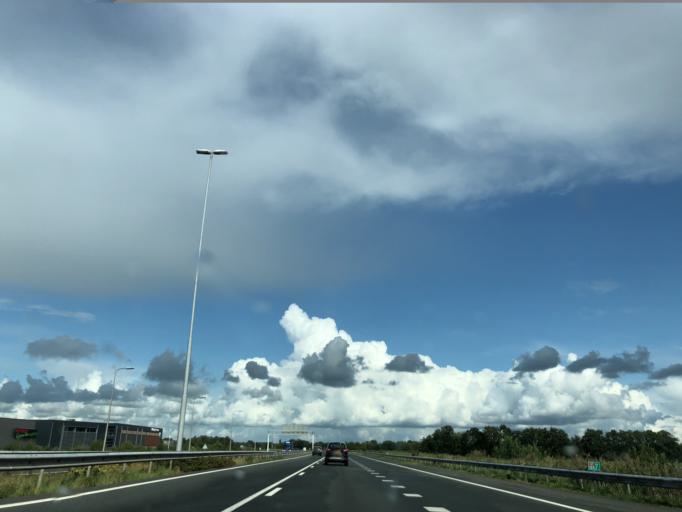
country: NL
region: Friesland
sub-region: Gemeente Smallingerland
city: Drachtstercompagnie
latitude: 53.1066
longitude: 6.1398
